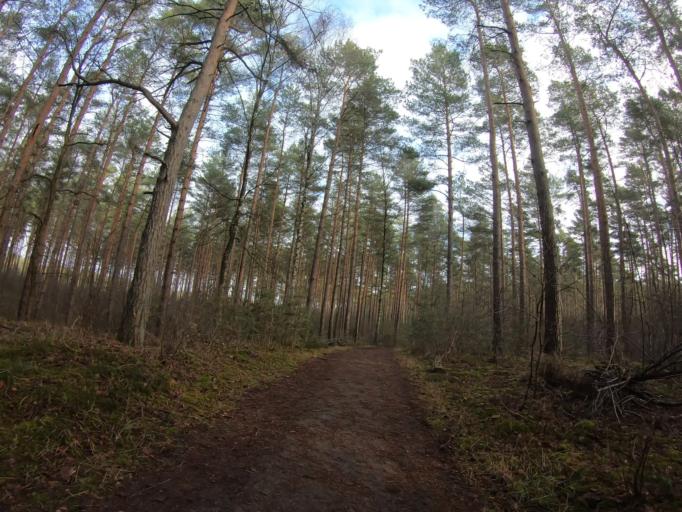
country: DE
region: Lower Saxony
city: Ribbesbuttel
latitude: 52.4795
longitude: 10.4984
